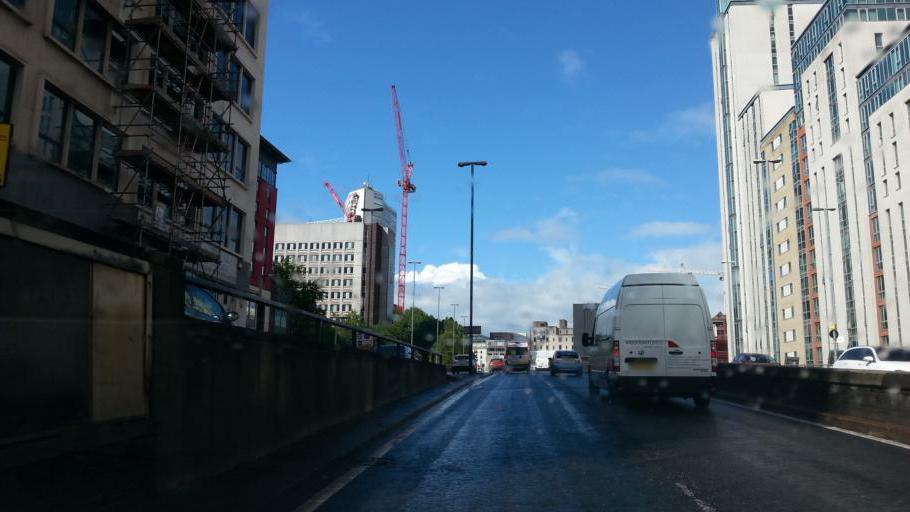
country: GB
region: England
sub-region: City and Borough of Birmingham
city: Birmingham
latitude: 52.4763
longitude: -1.9021
